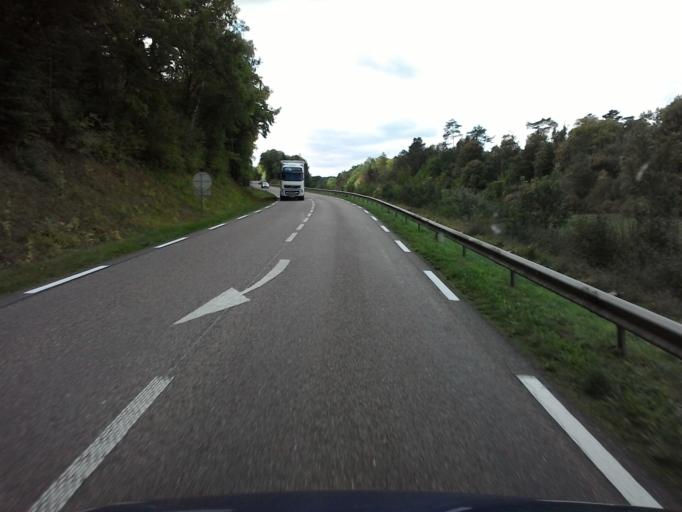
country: FR
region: Lorraine
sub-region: Departement des Vosges
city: Neufchateau
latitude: 48.3494
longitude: 5.6631
